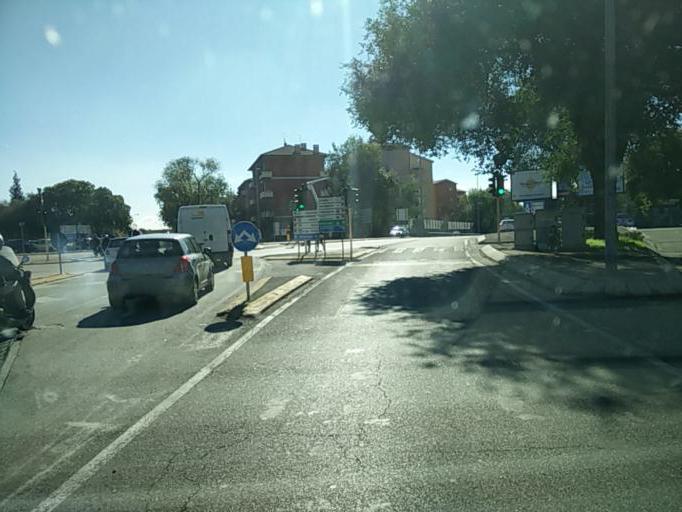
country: IT
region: Veneto
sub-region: Provincia di Verona
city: Verona
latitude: 45.4328
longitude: 10.9798
